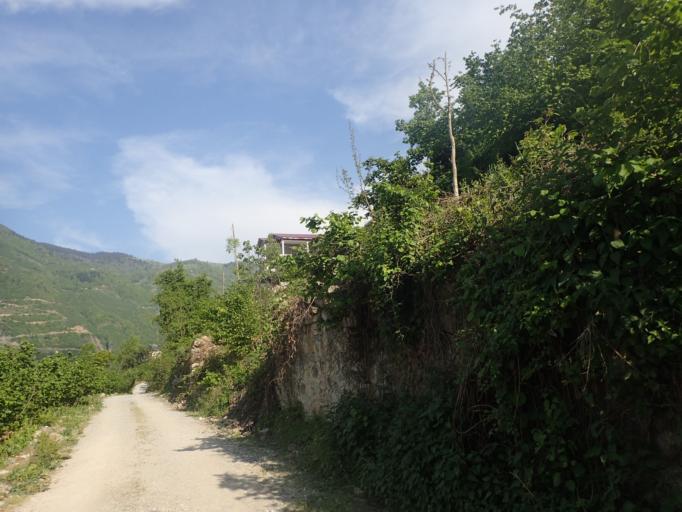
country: TR
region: Ordu
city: Topcam
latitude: 40.7090
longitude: 37.8665
